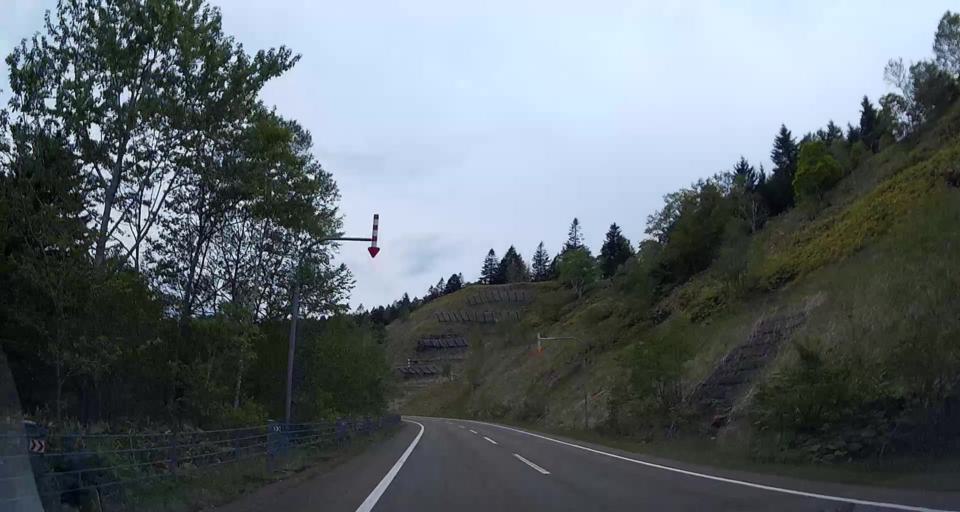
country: JP
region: Hokkaido
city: Shiraoi
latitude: 42.6778
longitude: 141.1271
